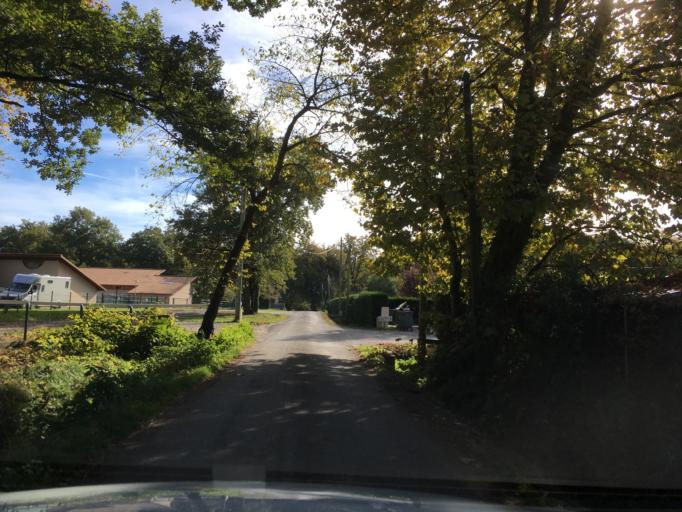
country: FR
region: Aquitaine
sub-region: Departement des Pyrenees-Atlantiques
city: Montardon
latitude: 43.3411
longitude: -0.3697
